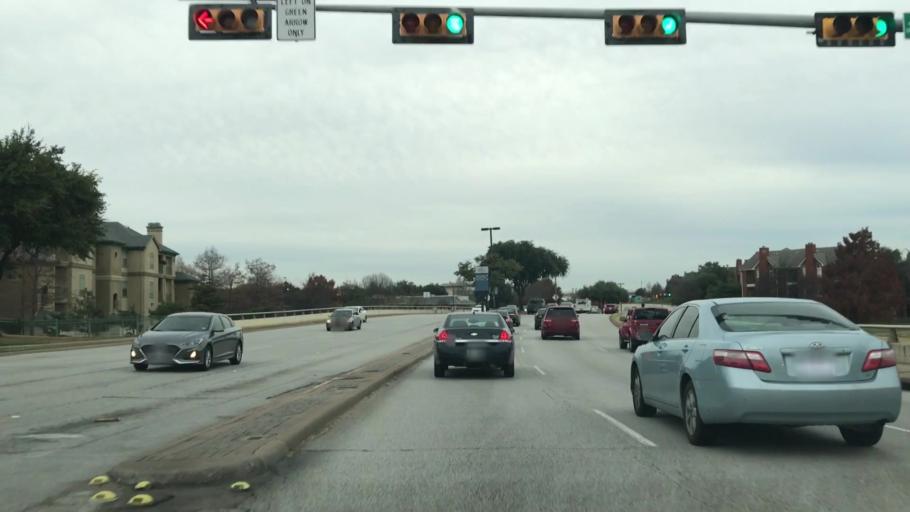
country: US
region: Texas
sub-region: Dallas County
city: Irving
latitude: 32.8804
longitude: -96.9634
